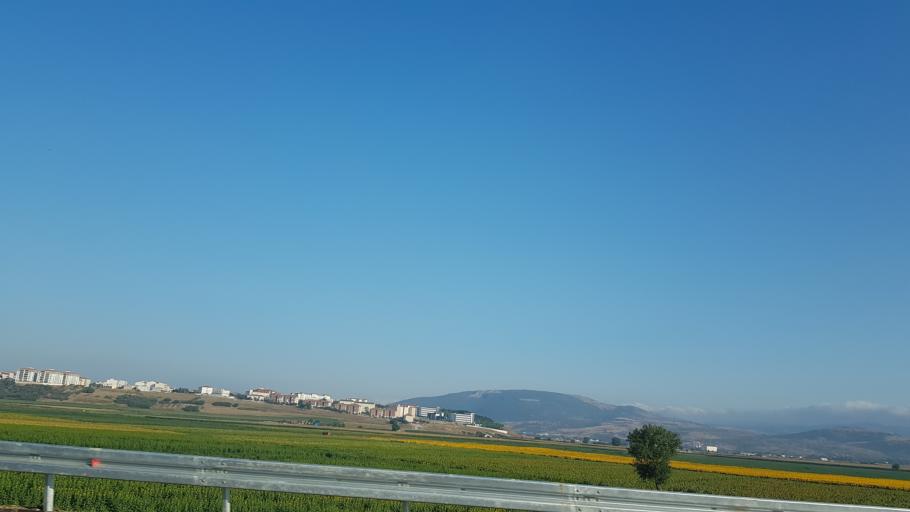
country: TR
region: Bursa
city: Karacabey
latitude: 40.2119
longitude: 28.3884
